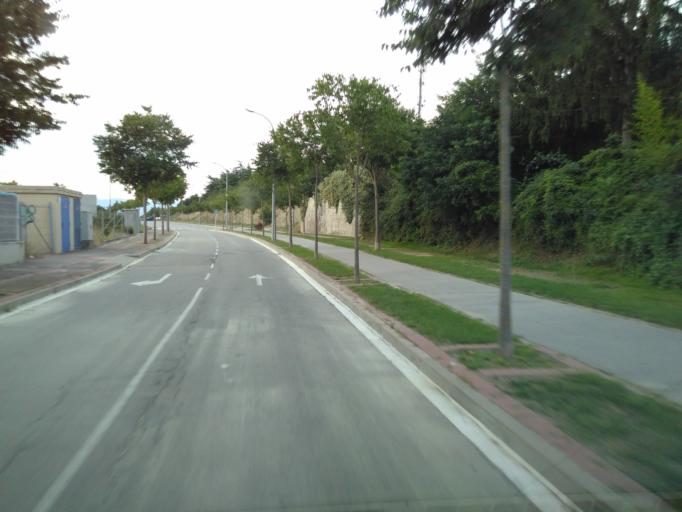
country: ES
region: Catalonia
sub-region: Provincia de Barcelona
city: Vic
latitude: 41.9397
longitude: 2.2575
